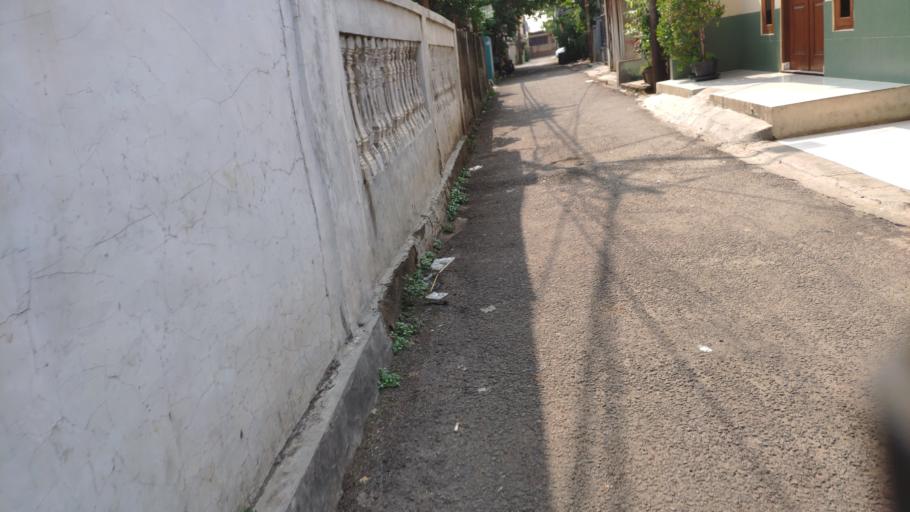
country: ID
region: West Java
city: Depok
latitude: -6.3202
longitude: 106.8184
